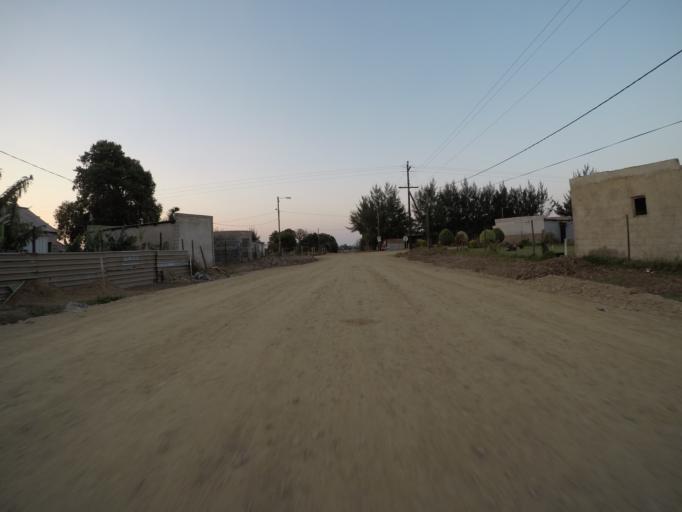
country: ZA
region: KwaZulu-Natal
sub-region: uThungulu District Municipality
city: Richards Bay
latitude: -28.7569
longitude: 32.1294
